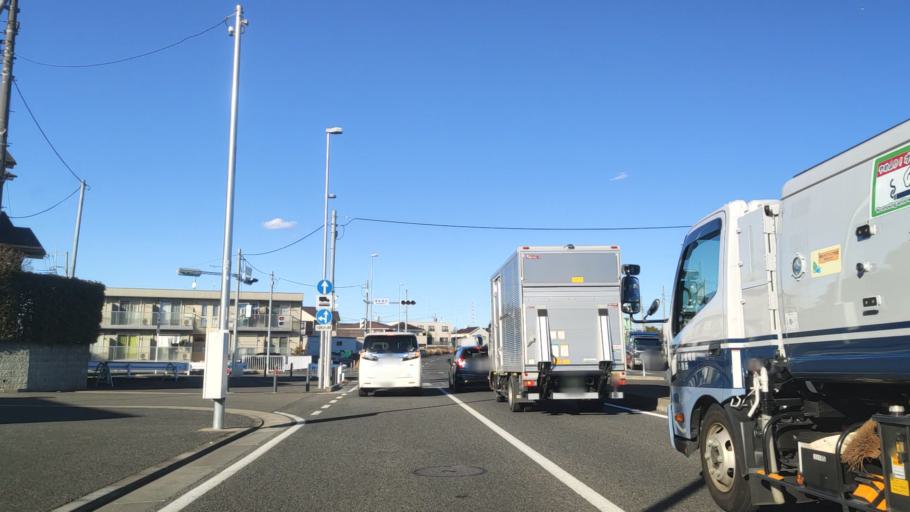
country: JP
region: Tokyo
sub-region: Machida-shi
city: Machida
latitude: 35.5241
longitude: 139.5456
